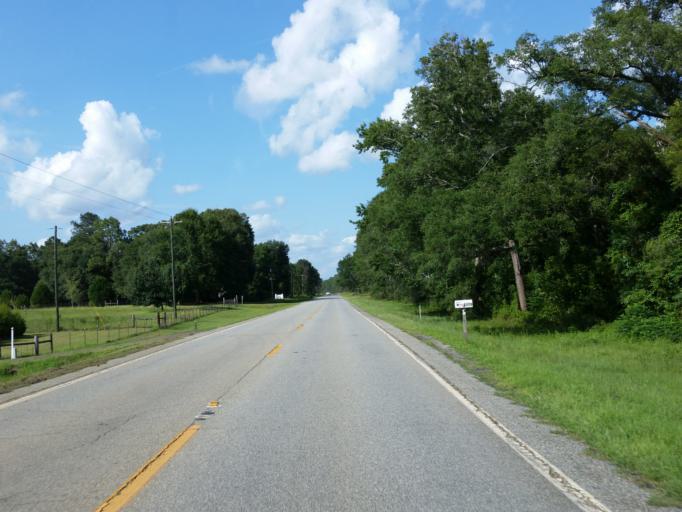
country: US
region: Georgia
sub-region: Lee County
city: Leesburg
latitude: 31.8521
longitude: -84.0833
